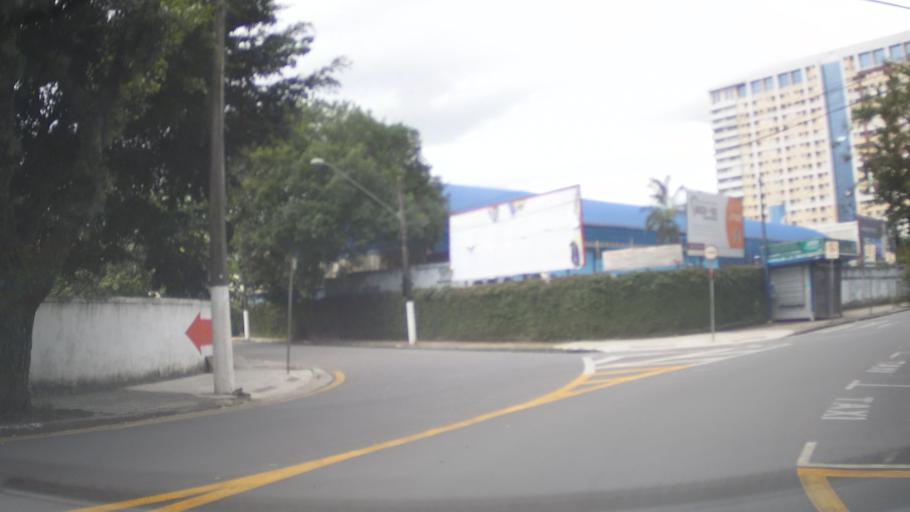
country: BR
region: Sao Paulo
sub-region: Santos
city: Santos
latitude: -23.9532
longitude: -46.3298
